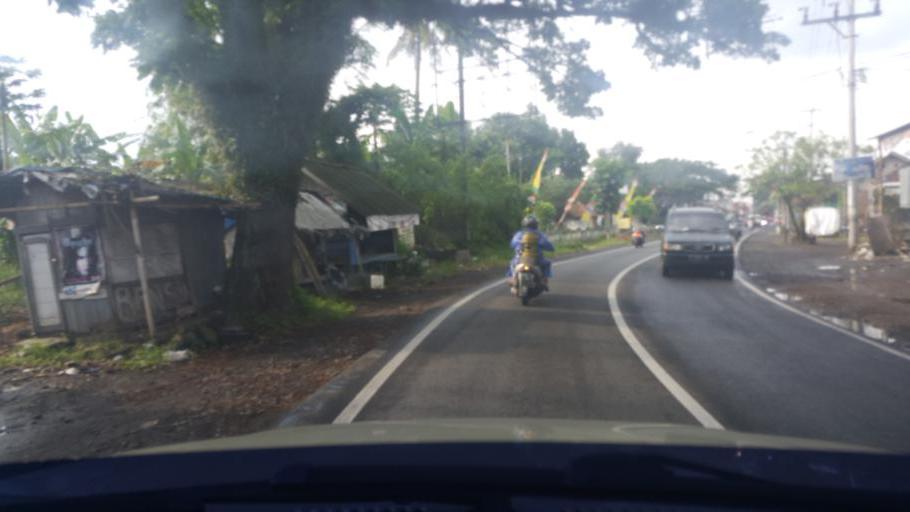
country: ID
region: West Java
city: Pakemitan
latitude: -7.2974
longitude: 108.2004
